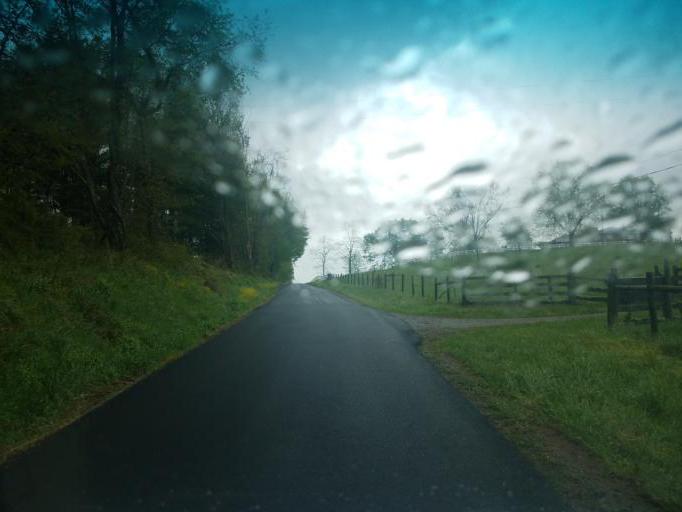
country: US
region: Virginia
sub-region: Smyth County
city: Marion
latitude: 36.9290
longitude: -81.5398
